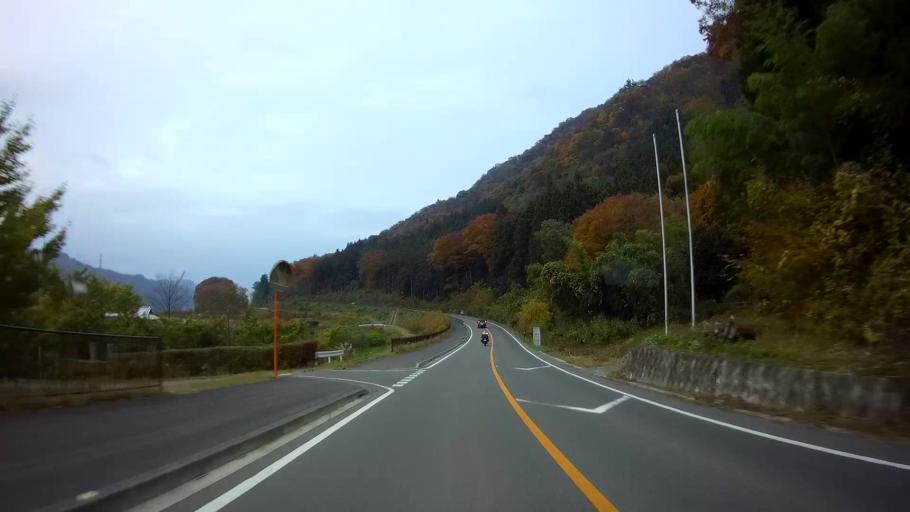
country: JP
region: Gunma
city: Nakanojomachi
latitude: 36.5678
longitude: 138.7350
